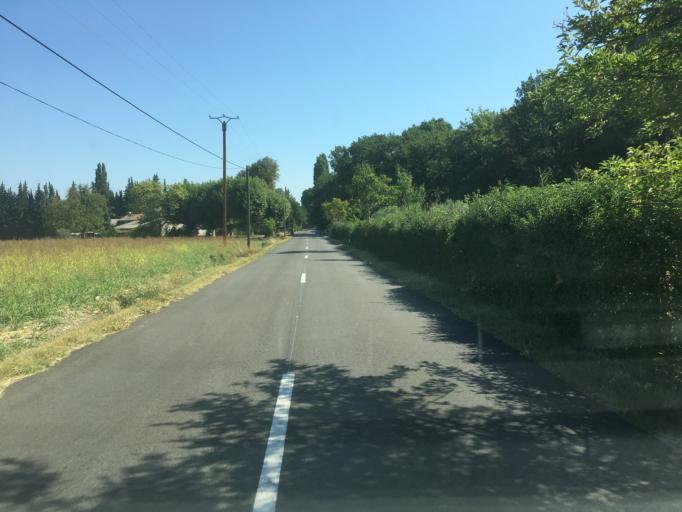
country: FR
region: Provence-Alpes-Cote d'Azur
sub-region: Departement des Alpes-de-Haute-Provence
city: Volx
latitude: 43.8521
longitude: 5.8824
